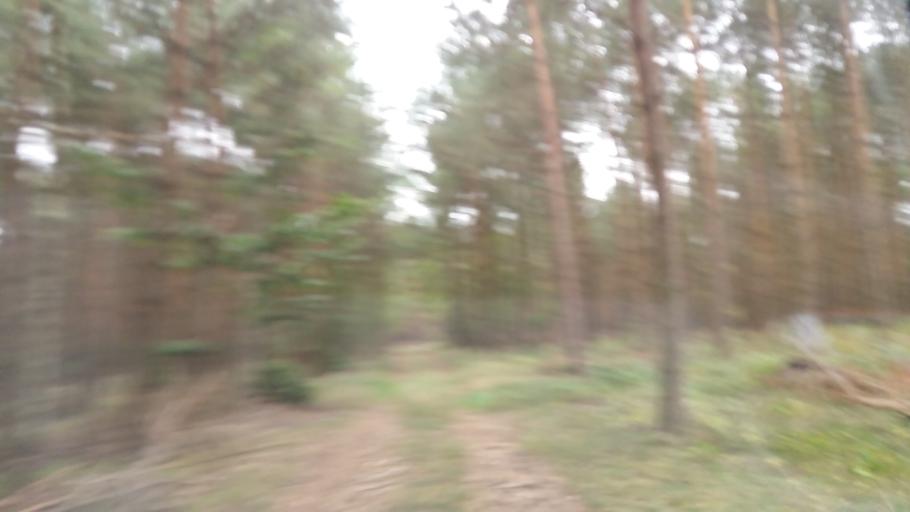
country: PL
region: West Pomeranian Voivodeship
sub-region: Powiat choszczenski
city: Bierzwnik
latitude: 52.9883
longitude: 15.5984
